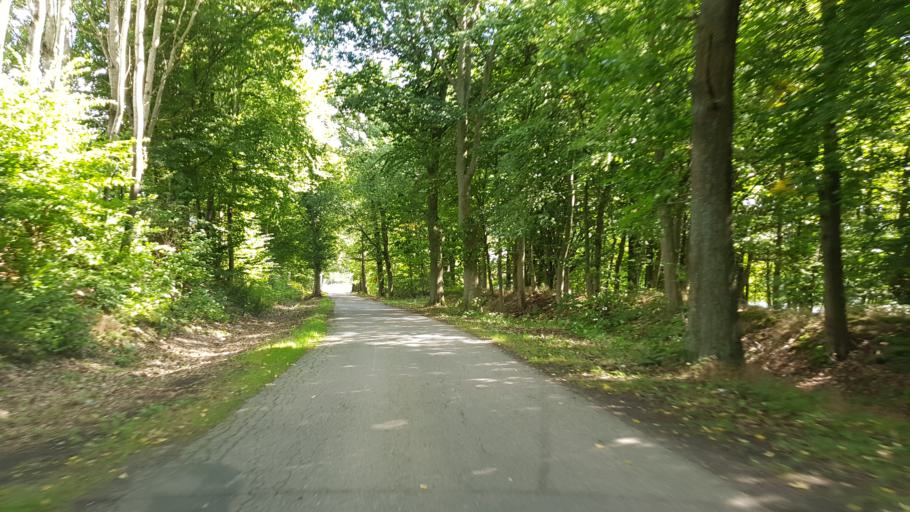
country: PL
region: West Pomeranian Voivodeship
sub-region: Powiat bialogardzki
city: Tychowo
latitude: 53.9823
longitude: 16.3068
